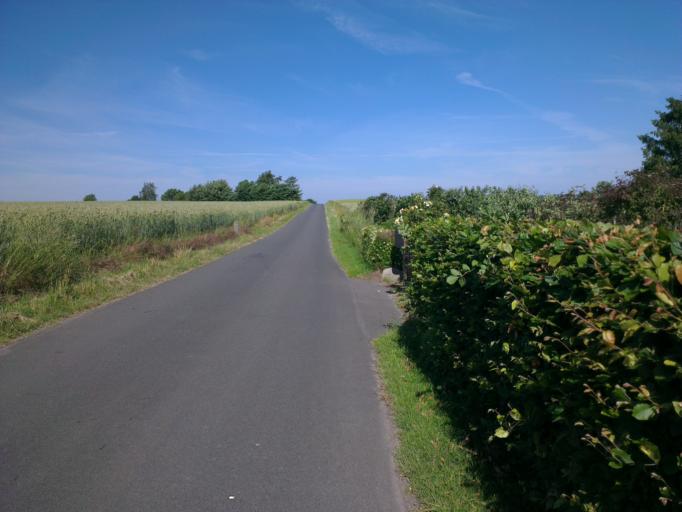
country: DK
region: Capital Region
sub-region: Frederikssund Kommune
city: Skibby
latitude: 55.7862
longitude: 11.8739
